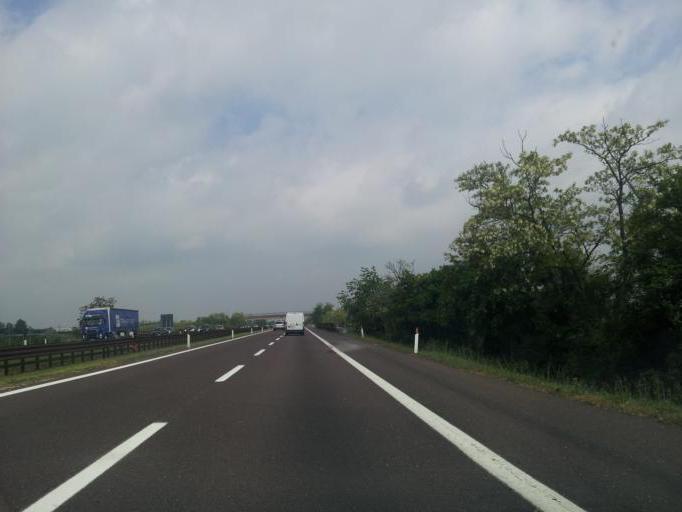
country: IT
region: Veneto
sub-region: Provincia di Verona
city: Alpo
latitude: 45.3790
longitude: 10.9129
